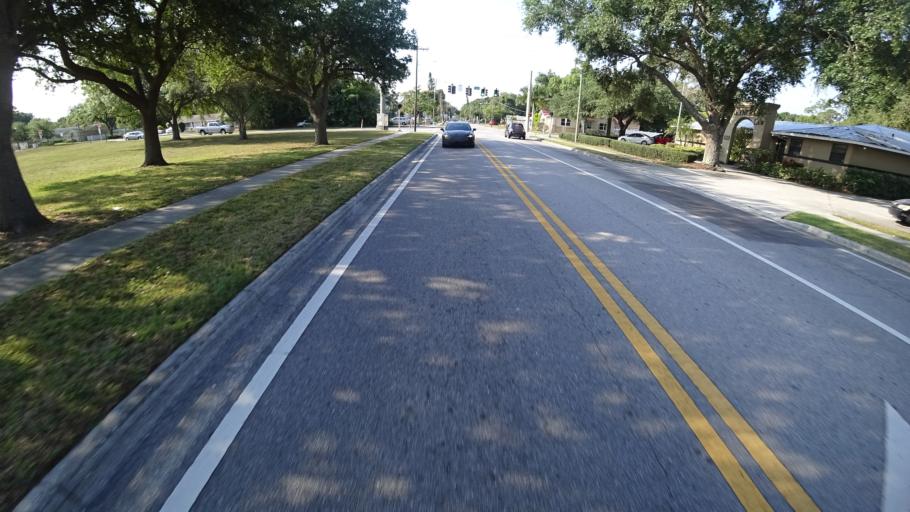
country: US
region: Florida
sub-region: Manatee County
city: West Bradenton
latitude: 27.4926
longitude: -82.6039
